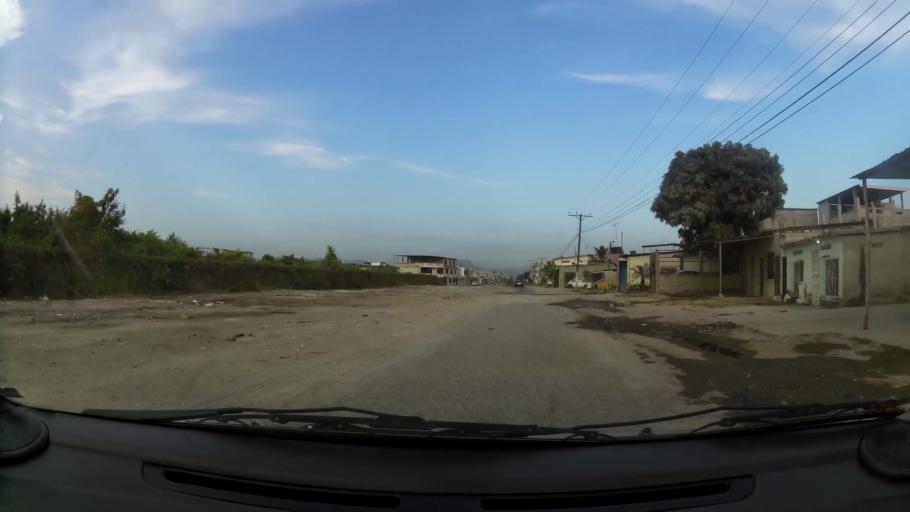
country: EC
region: Guayas
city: Eloy Alfaro
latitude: -2.0957
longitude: -79.9041
